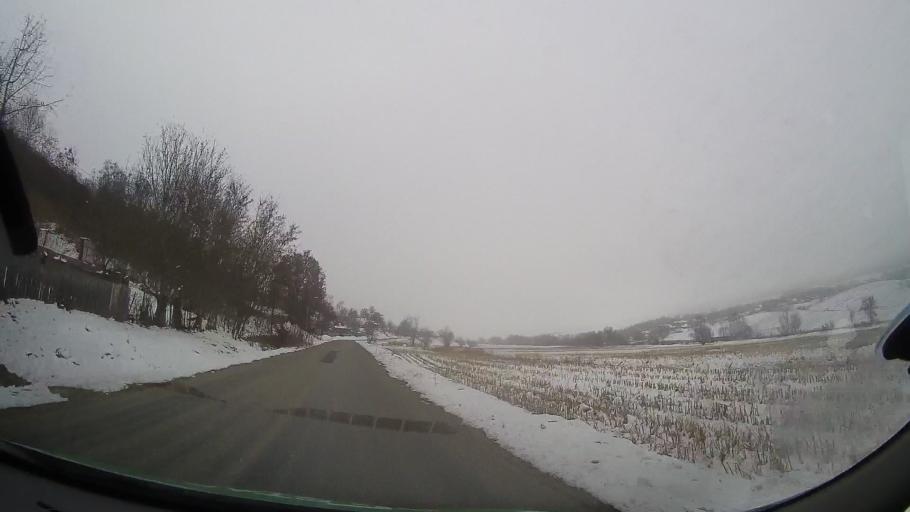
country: RO
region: Bacau
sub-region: Comuna Vultureni
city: Vultureni
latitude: 46.3346
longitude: 27.2913
